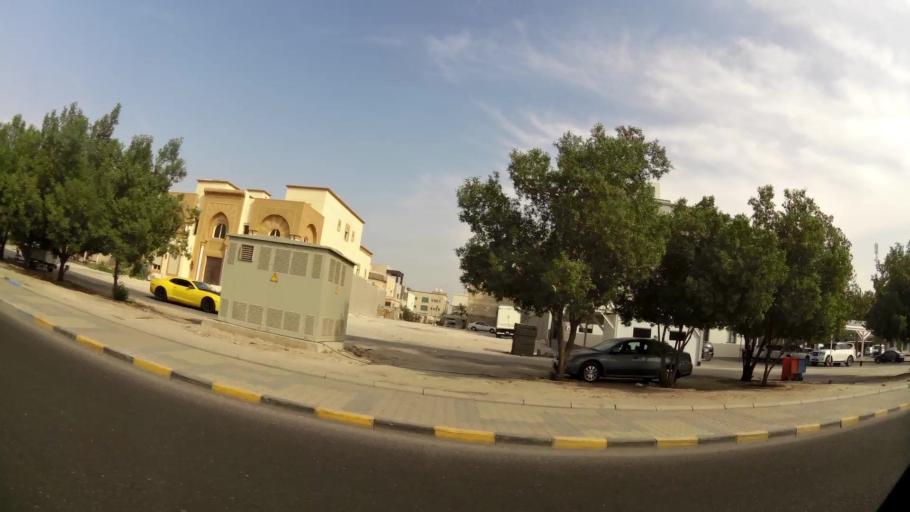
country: KW
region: Al Asimah
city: Ash Shamiyah
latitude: 29.3303
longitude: 47.9620
